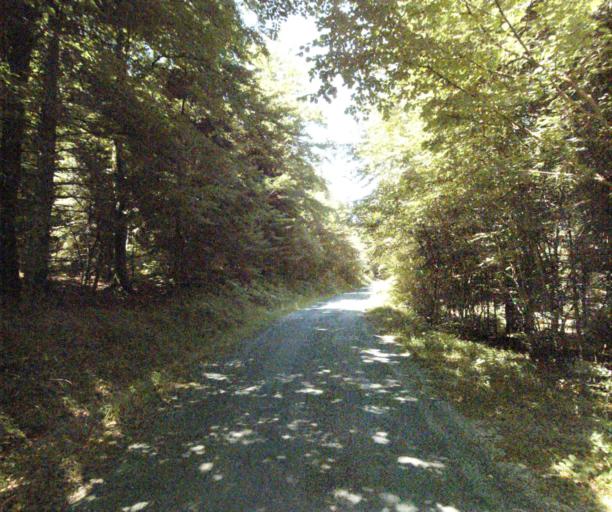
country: FR
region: Languedoc-Roussillon
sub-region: Departement de l'Aude
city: Cuxac-Cabardes
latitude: 43.3995
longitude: 2.2200
